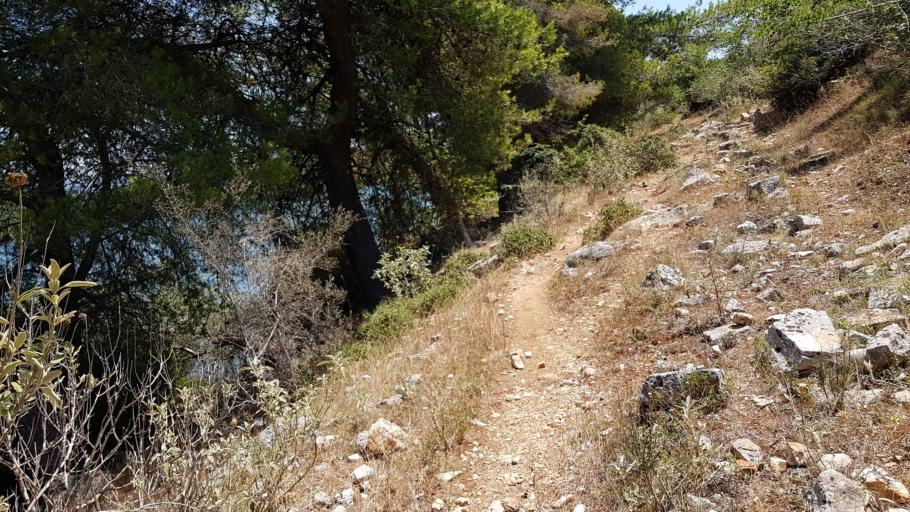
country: AL
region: Vlore
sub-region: Rrethi i Sarandes
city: Xarre
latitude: 39.7483
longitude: 19.9898
